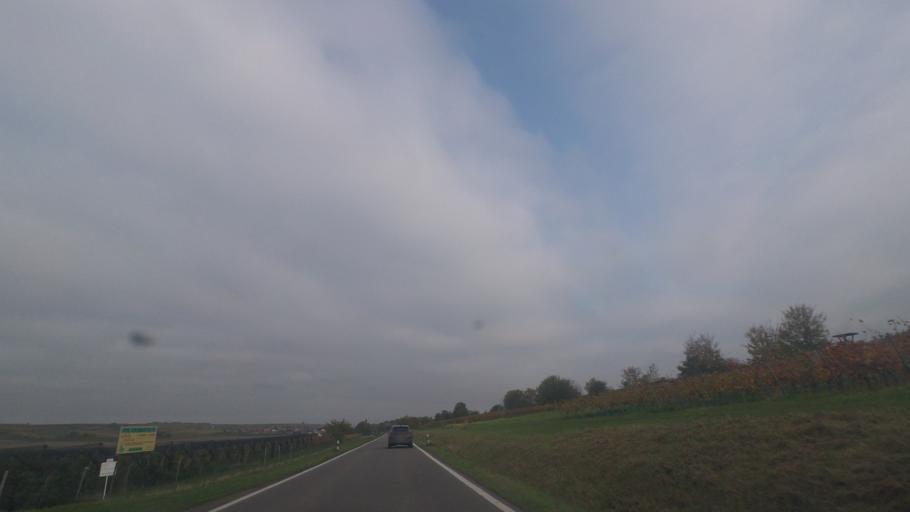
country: DE
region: Rheinland-Pfalz
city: Bechtheim
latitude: 49.7234
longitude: 8.2738
